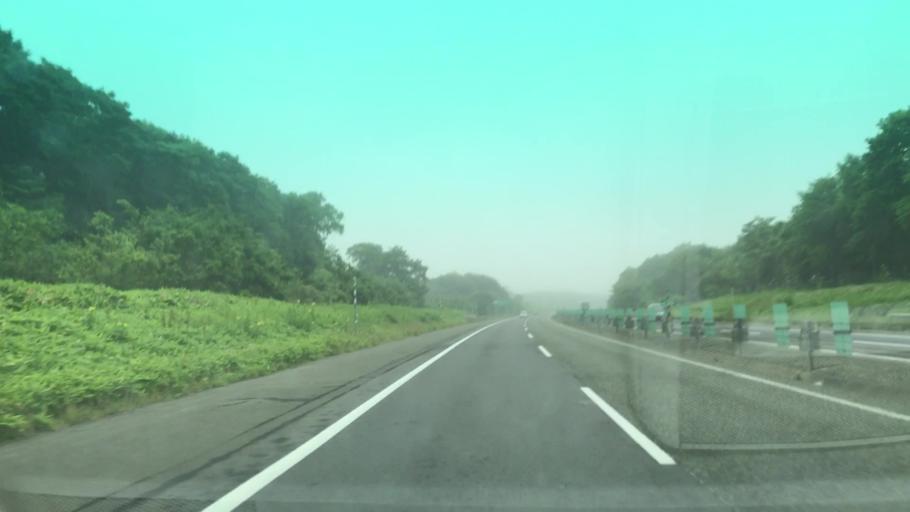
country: JP
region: Hokkaido
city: Chitose
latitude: 42.8318
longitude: 141.6111
